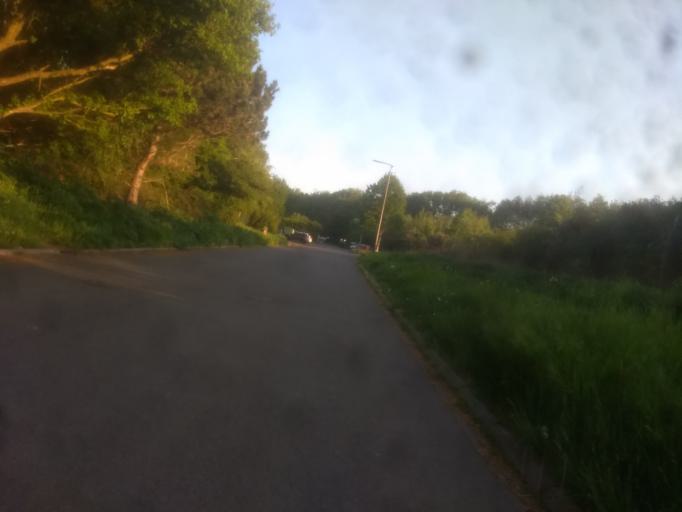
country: FR
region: Nord-Pas-de-Calais
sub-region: Departement du Pas-de-Calais
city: Saint-Laurent-Blangy
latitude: 50.2921
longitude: 2.8135
